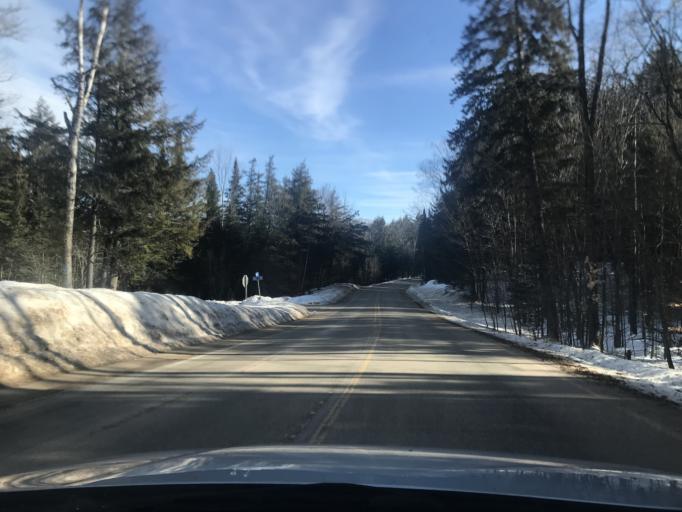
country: US
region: Michigan
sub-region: Dickinson County
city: Kingsford
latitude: 45.4103
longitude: -88.3571
